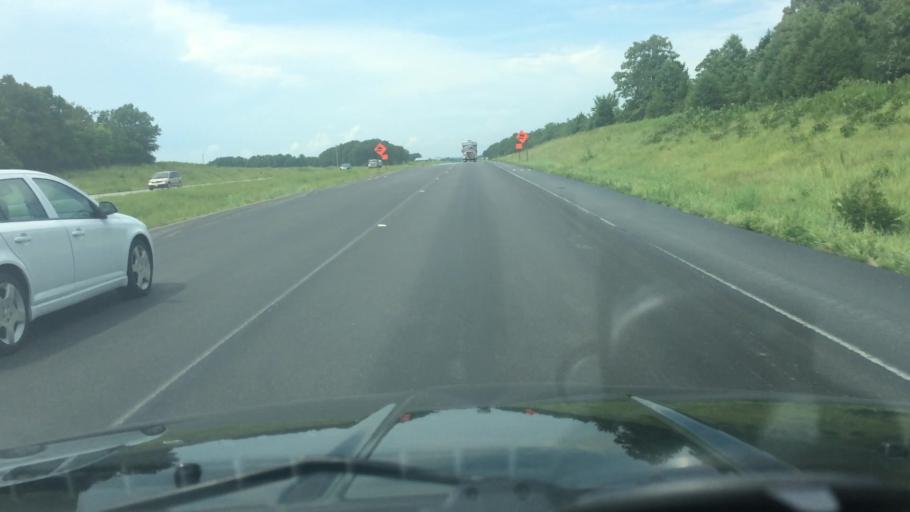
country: US
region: Missouri
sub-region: Saint Clair County
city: Osceola
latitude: 37.9648
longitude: -93.6446
